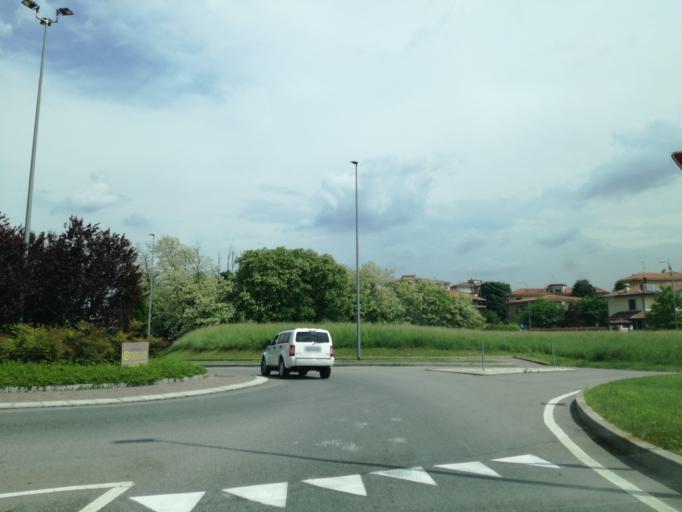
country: IT
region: Lombardy
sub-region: Provincia di Monza e Brianza
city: Carate Brianza
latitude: 45.6727
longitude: 9.2402
